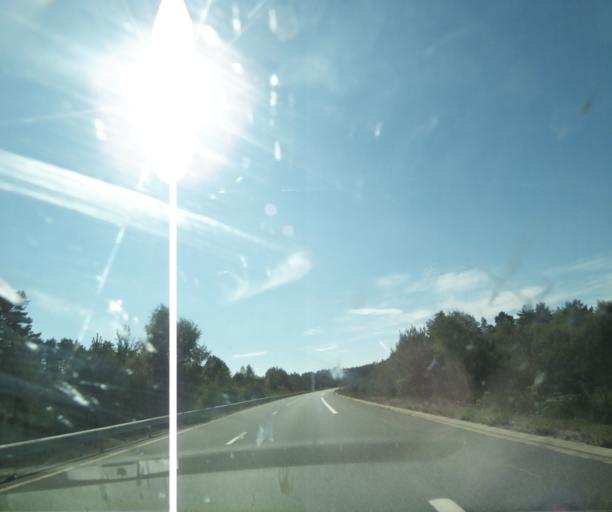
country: FR
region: Limousin
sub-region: Departement de la Correze
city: Correze
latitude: 45.3618
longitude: 1.9469
